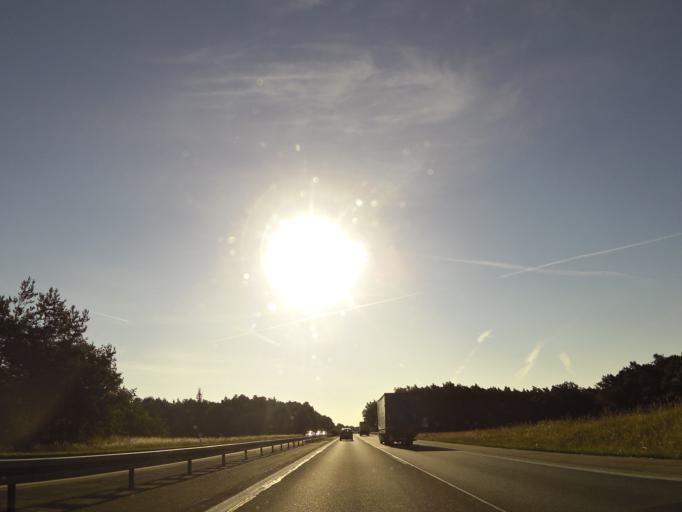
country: DE
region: Bavaria
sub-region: Regierungsbezirk Mittelfranken
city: Muhlhausen
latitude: 49.7375
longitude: 10.7729
